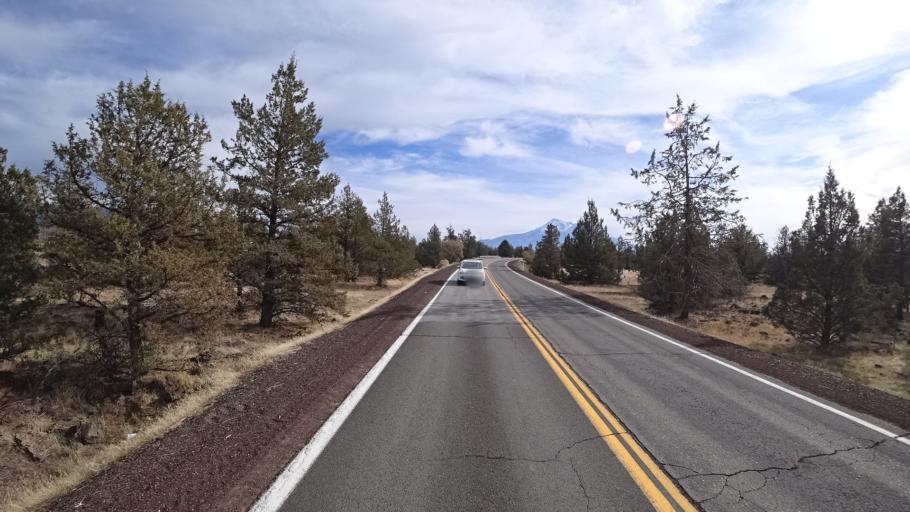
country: US
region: California
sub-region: Siskiyou County
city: Montague
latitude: 41.6069
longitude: -122.3962
